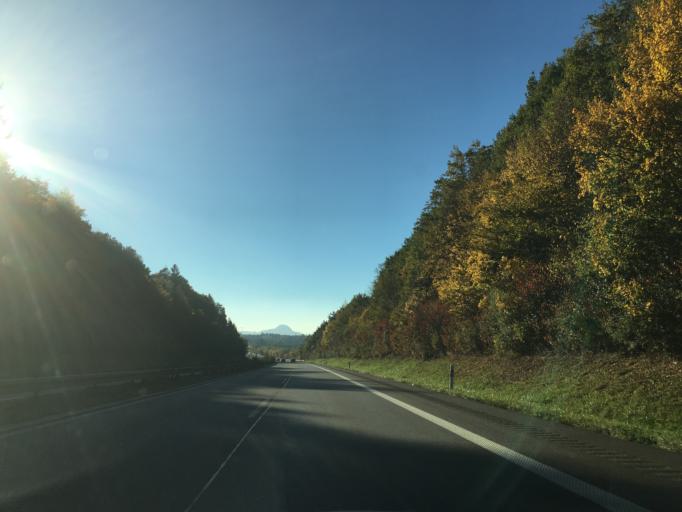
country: DE
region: Baden-Wuerttemberg
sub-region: Freiburg Region
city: Steisslingen
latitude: 47.7718
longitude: 8.9477
